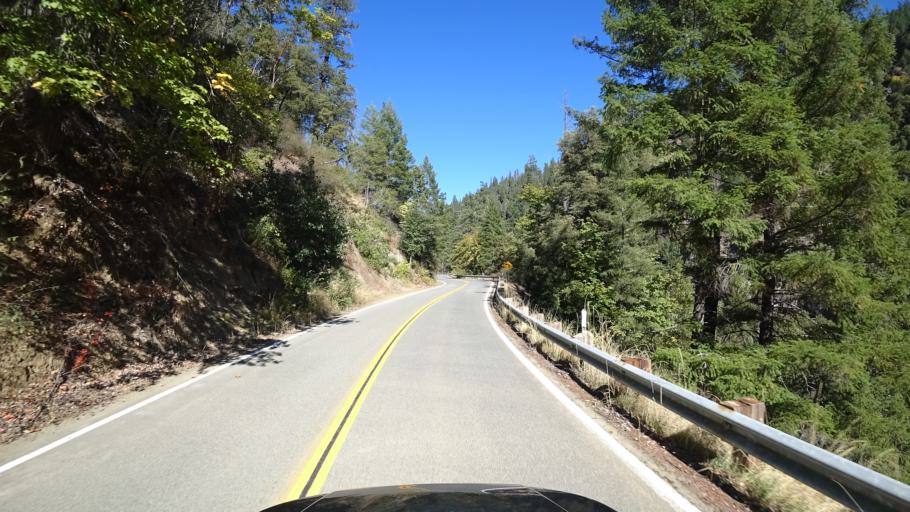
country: US
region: California
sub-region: Siskiyou County
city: Happy Camp
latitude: 41.3551
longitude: -123.4087
